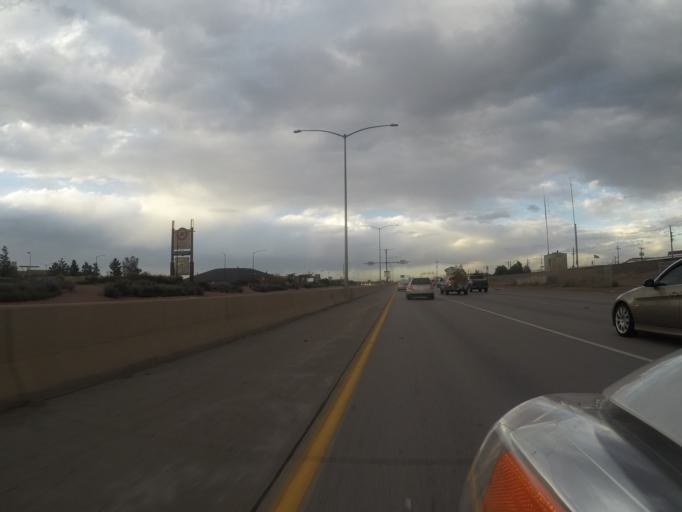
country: US
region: Colorado
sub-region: Arapahoe County
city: Englewood
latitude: 39.6474
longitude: -105.0038
